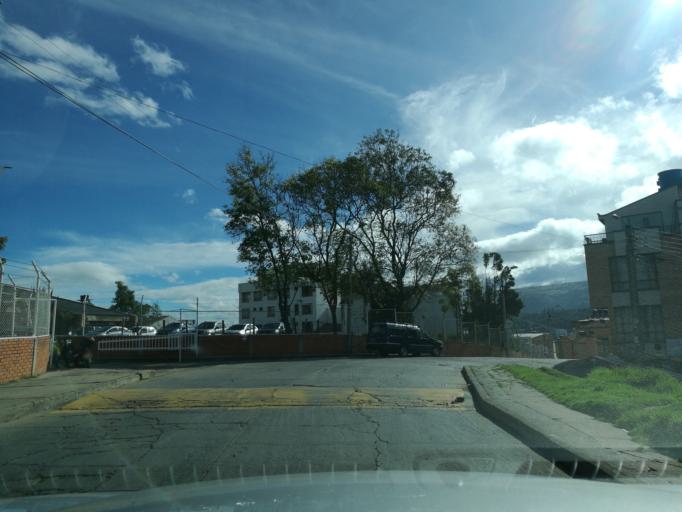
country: CO
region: Boyaca
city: Tunja
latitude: 5.5553
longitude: -73.3539
